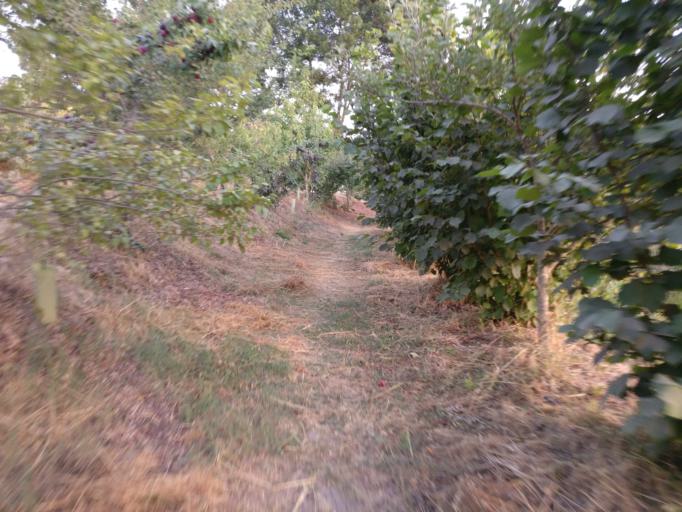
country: PT
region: Beja
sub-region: Odemira
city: Odemira
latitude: 37.7177
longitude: -8.5181
